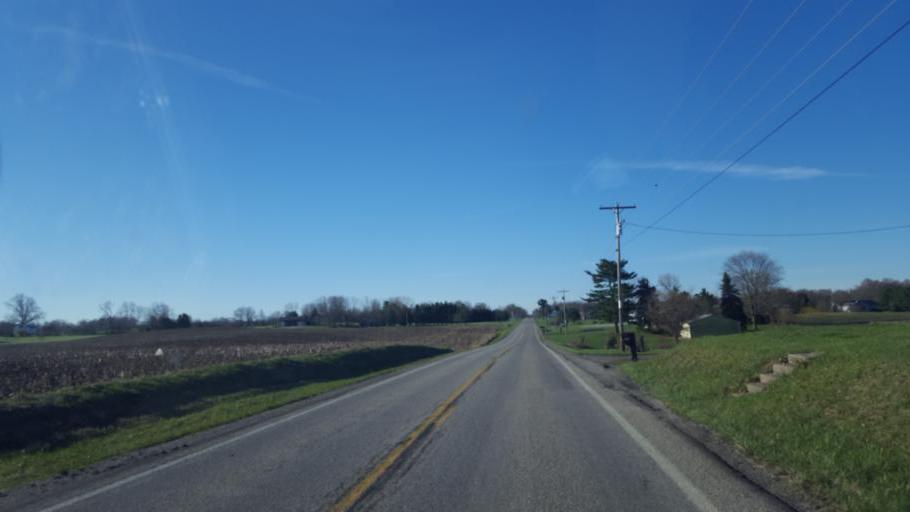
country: US
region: Ohio
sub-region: Morrow County
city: Mount Gilead
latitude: 40.5195
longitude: -82.8168
